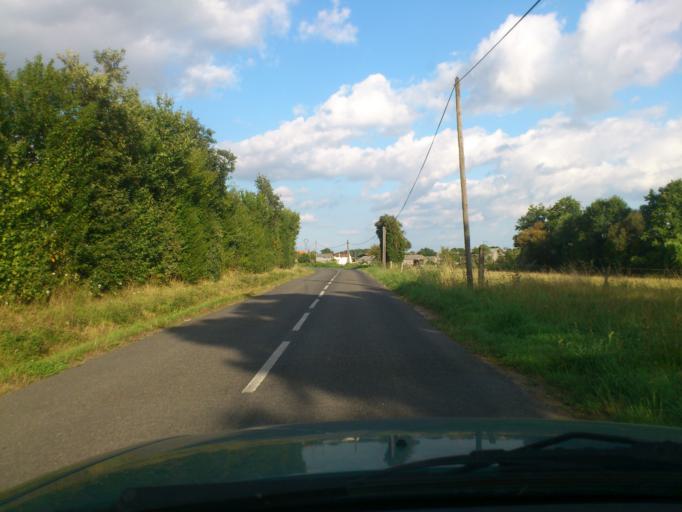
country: FR
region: Pays de la Loire
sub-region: Departement de la Loire-Atlantique
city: La Planche
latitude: 47.0085
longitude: -1.4241
